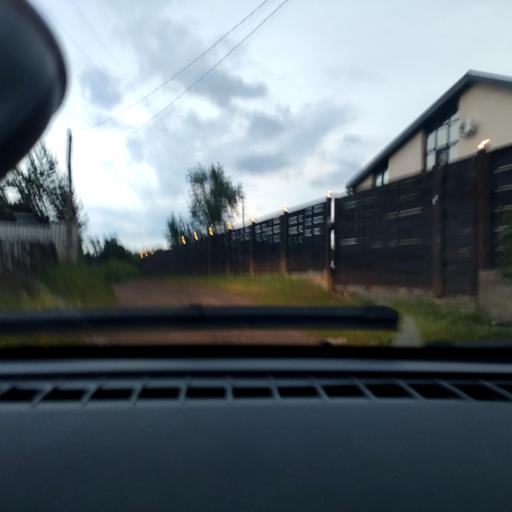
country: RU
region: Samara
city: Samara
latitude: 53.1276
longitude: 50.1877
